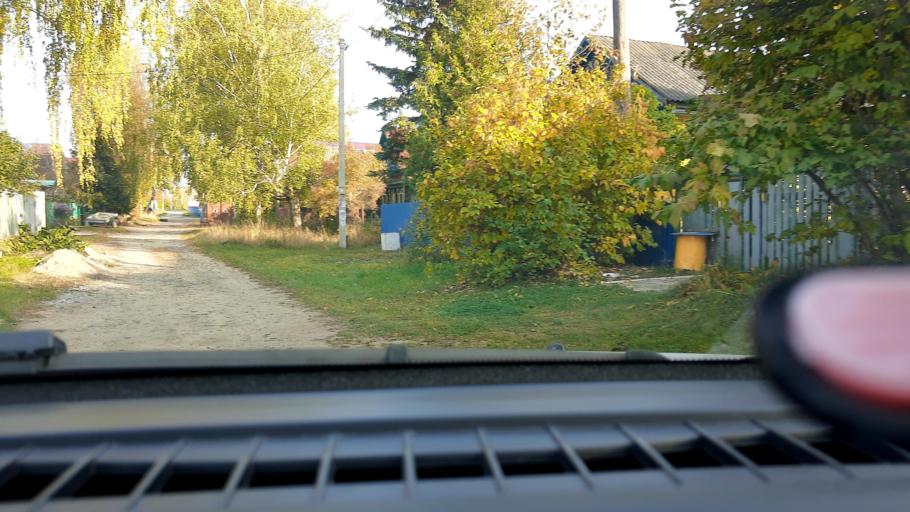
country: RU
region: Nizjnij Novgorod
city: Lukino
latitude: 56.3881
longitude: 43.7464
